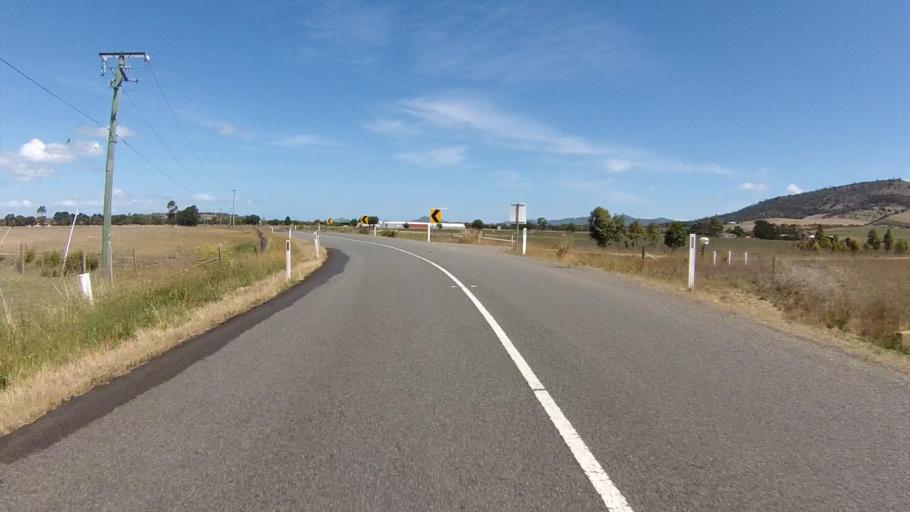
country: AU
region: Tasmania
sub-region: Sorell
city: Sorell
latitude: -42.7678
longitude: 147.5174
